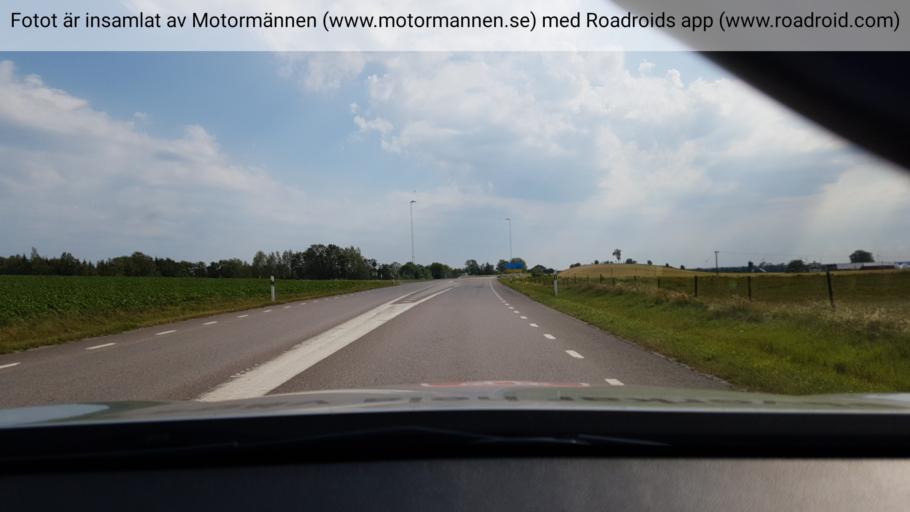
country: SE
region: Vaestra Goetaland
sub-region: Falkopings Kommun
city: Falkoeping
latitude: 58.1363
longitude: 13.5630
